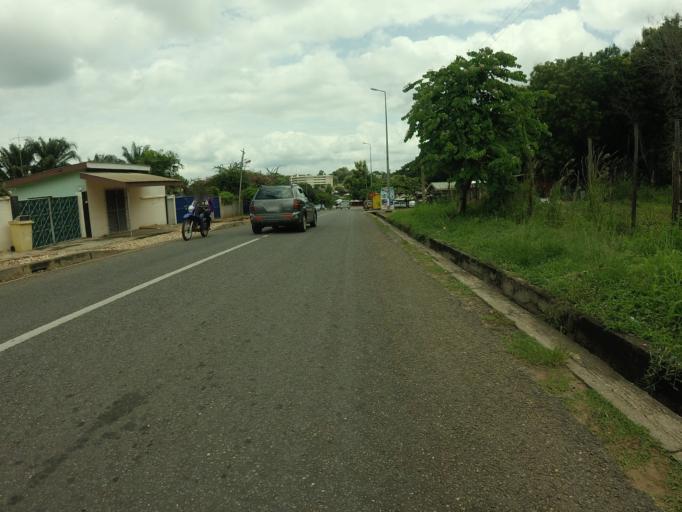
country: GH
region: Volta
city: Ho
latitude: 6.5935
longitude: 0.4737
